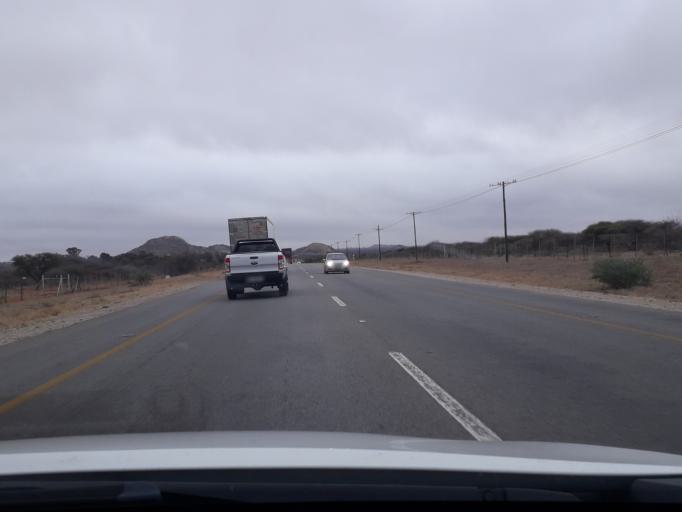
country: ZA
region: Limpopo
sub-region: Capricorn District Municipality
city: Mankoeng
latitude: -23.5498
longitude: 29.6910
